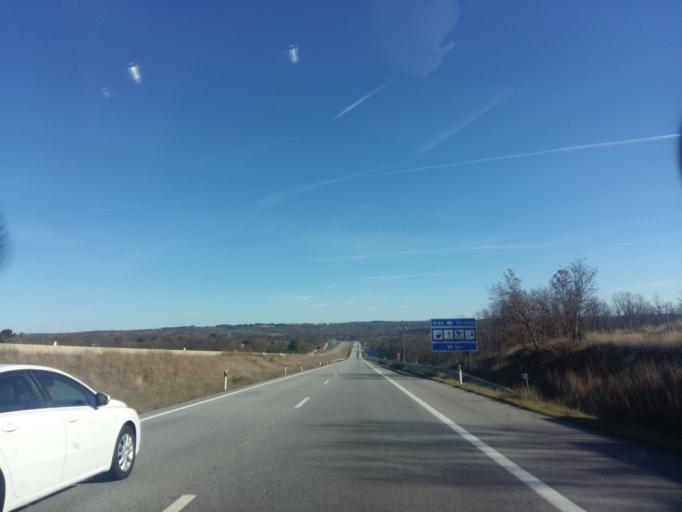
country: PT
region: Guarda
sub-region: Pinhel
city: Pinhel
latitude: 40.6043
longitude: -7.0609
